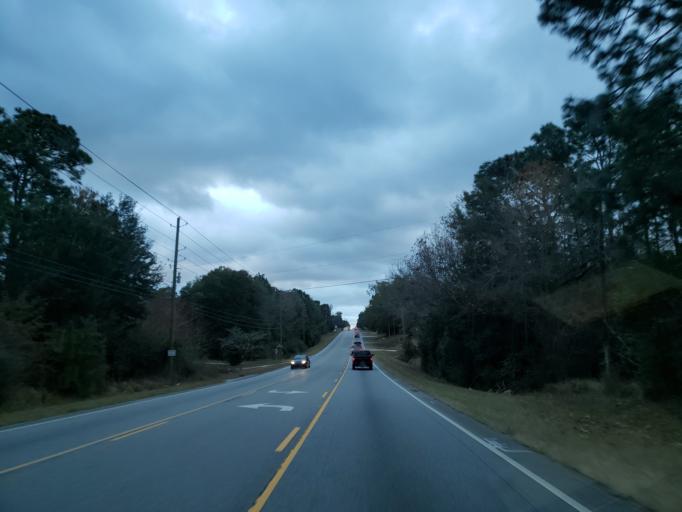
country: US
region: Mississippi
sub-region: Jackson County
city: Hurley
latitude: 30.7939
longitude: -88.3109
